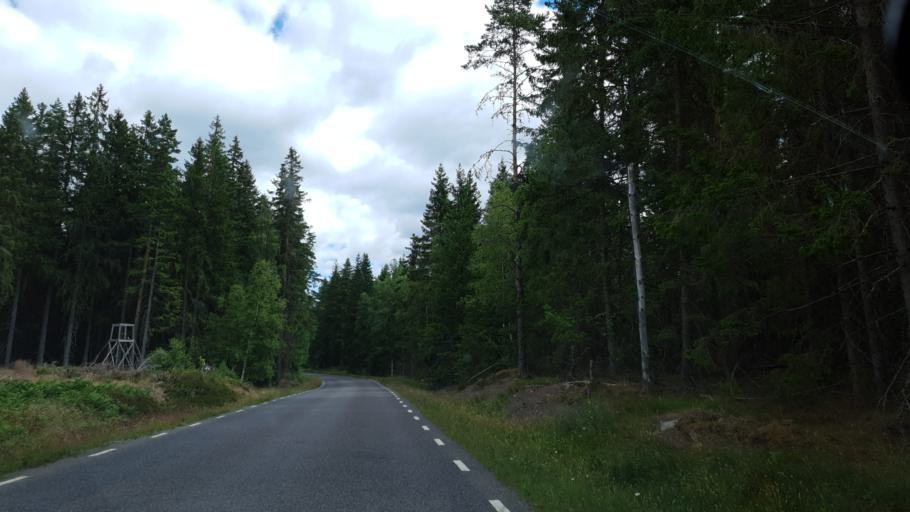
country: SE
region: Kronoberg
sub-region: Uppvidinge Kommun
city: Aseda
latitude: 57.1893
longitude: 15.3910
